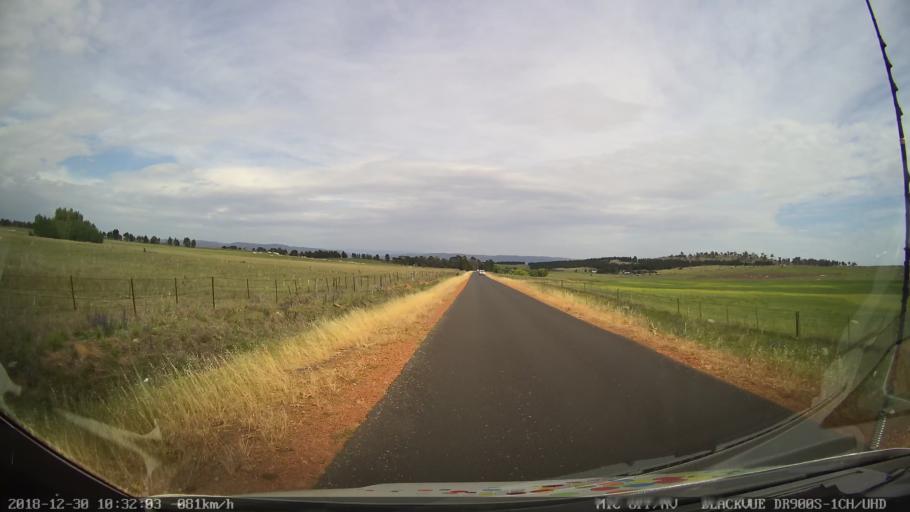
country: AU
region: New South Wales
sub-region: Snowy River
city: Berridale
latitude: -36.5030
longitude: 148.8713
